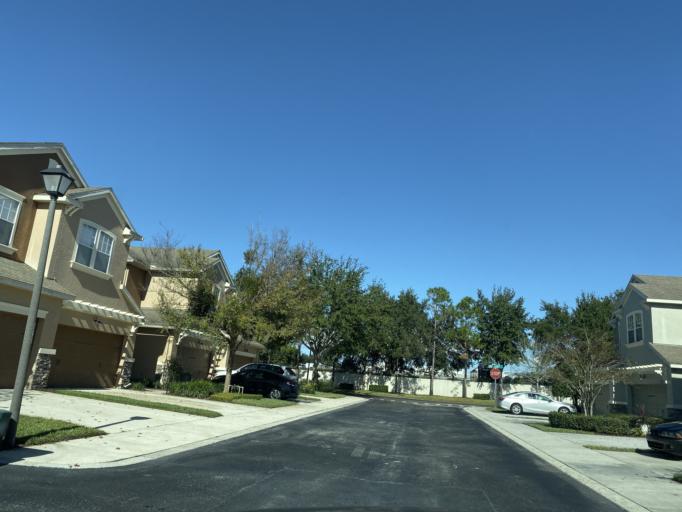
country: US
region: Florida
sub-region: Seminole County
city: Goldenrod
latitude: 28.6156
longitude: -81.2636
